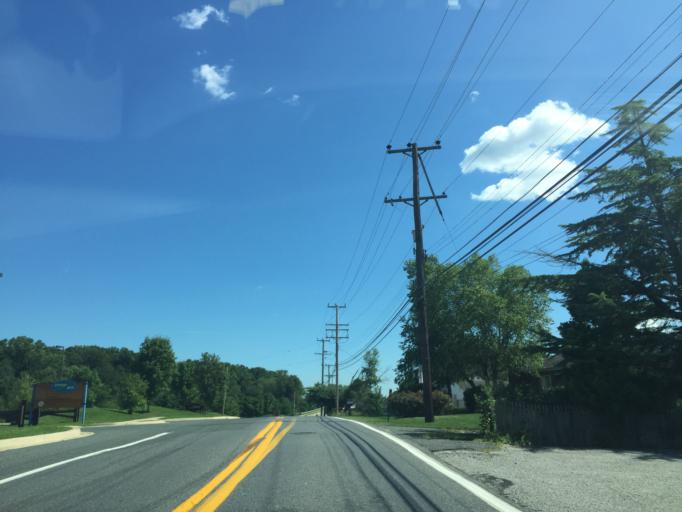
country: US
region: Maryland
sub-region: Baltimore County
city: White Marsh
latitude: 39.3926
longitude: -76.4411
